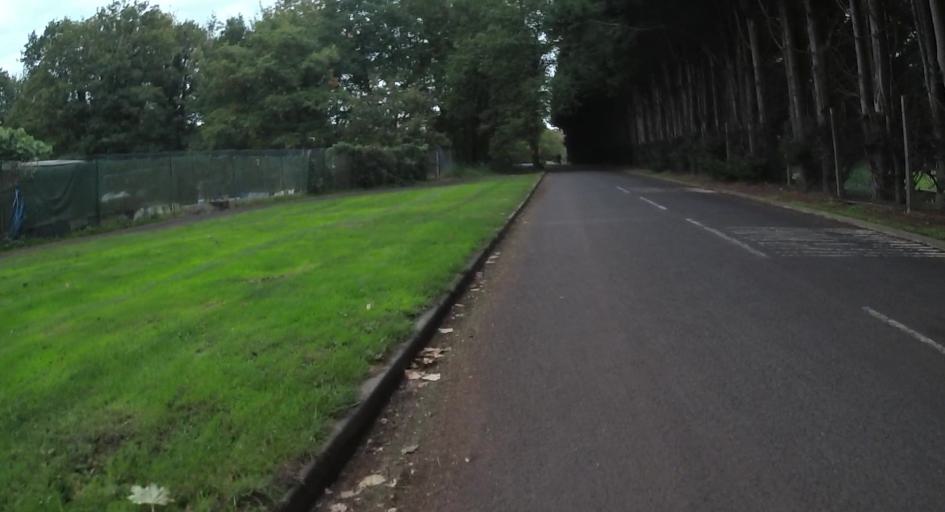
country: GB
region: England
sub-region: Bracknell Forest
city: Crowthorne
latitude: 51.3936
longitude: -0.7806
